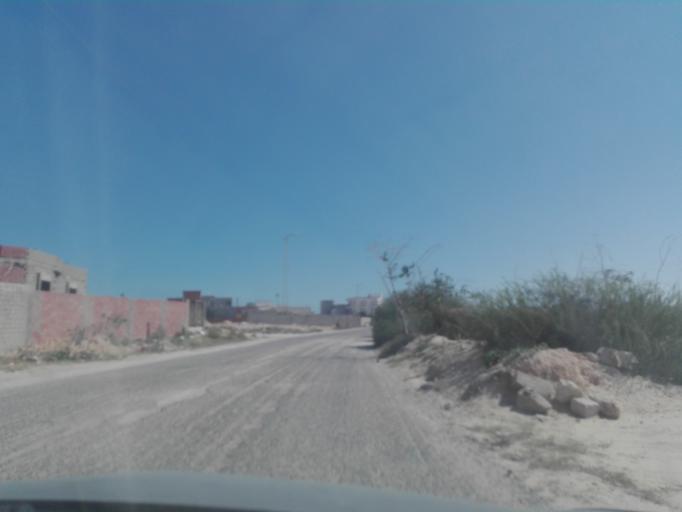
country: TN
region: Qabis
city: Gabes
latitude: 33.8705
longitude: 10.0460
